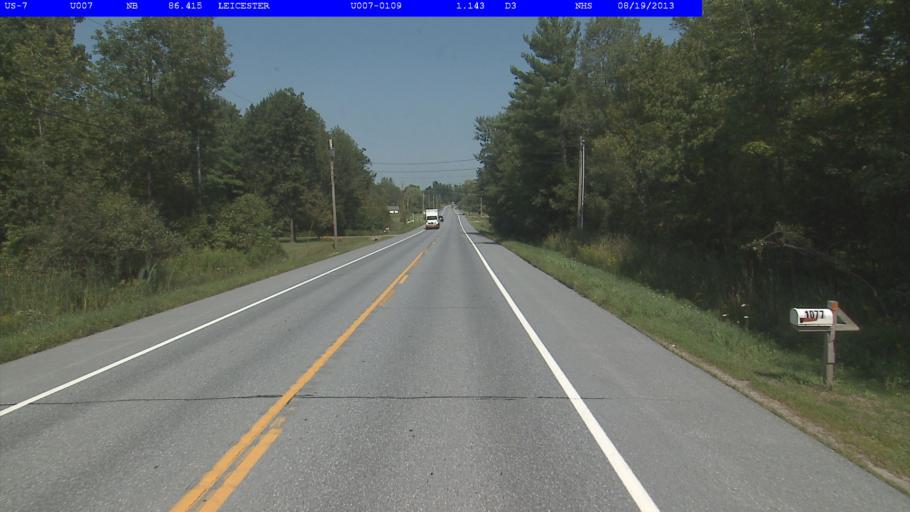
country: US
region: Vermont
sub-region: Rutland County
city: Brandon
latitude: 43.8598
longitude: -73.1065
